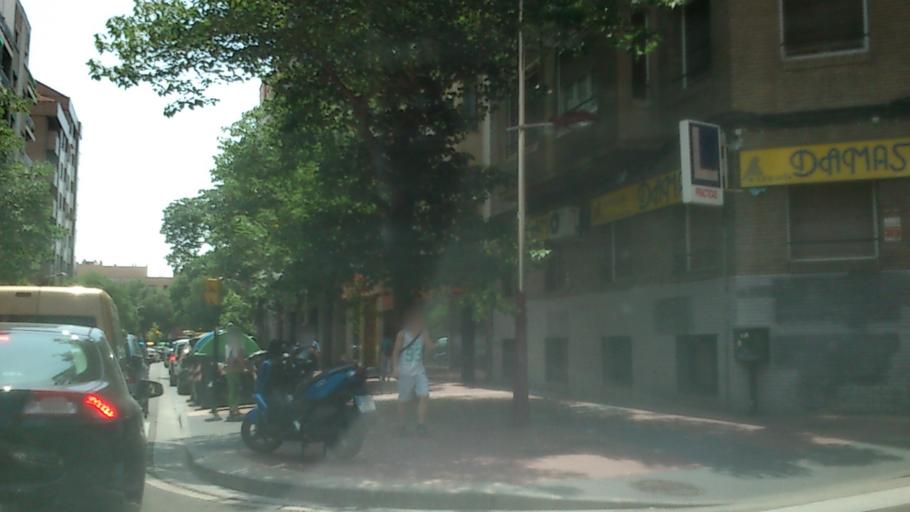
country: ES
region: Aragon
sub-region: Provincia de Zaragoza
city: Zaragoza
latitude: 41.6440
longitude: -0.8831
